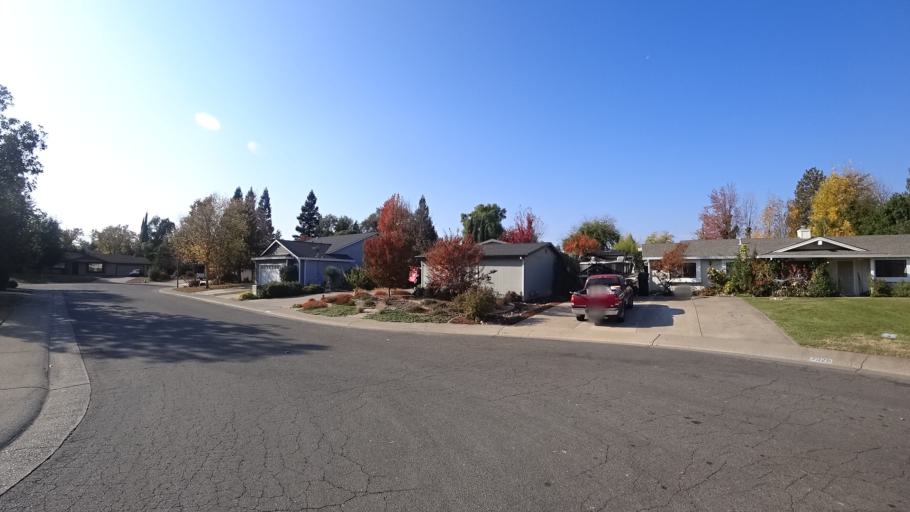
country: US
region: California
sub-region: Sacramento County
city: Citrus Heights
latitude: 38.7113
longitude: -121.2679
